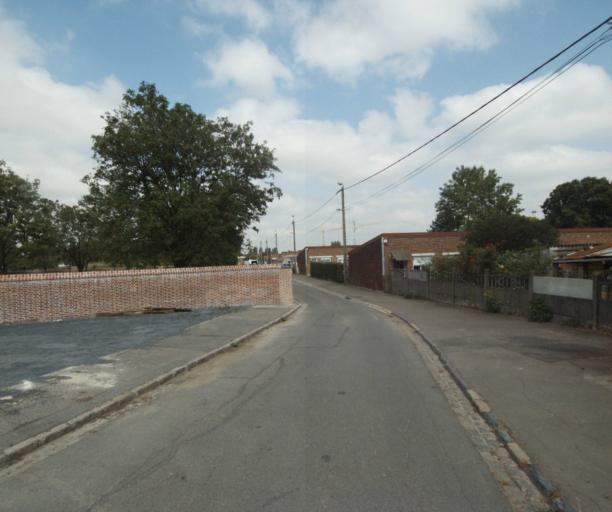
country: FR
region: Nord-Pas-de-Calais
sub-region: Departement du Nord
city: Armentieres
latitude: 50.6859
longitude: 2.8647
